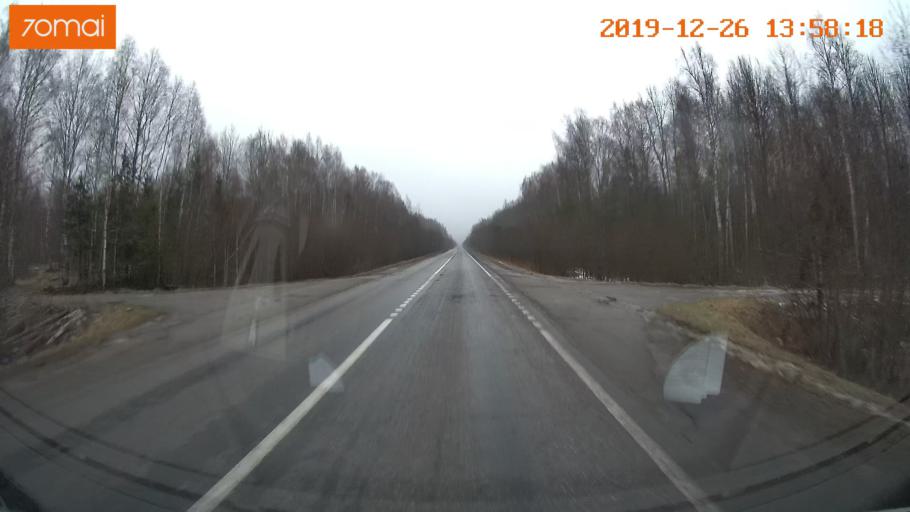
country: RU
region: Jaroslavl
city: Poshekhon'ye
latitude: 58.5752
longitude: 38.6979
